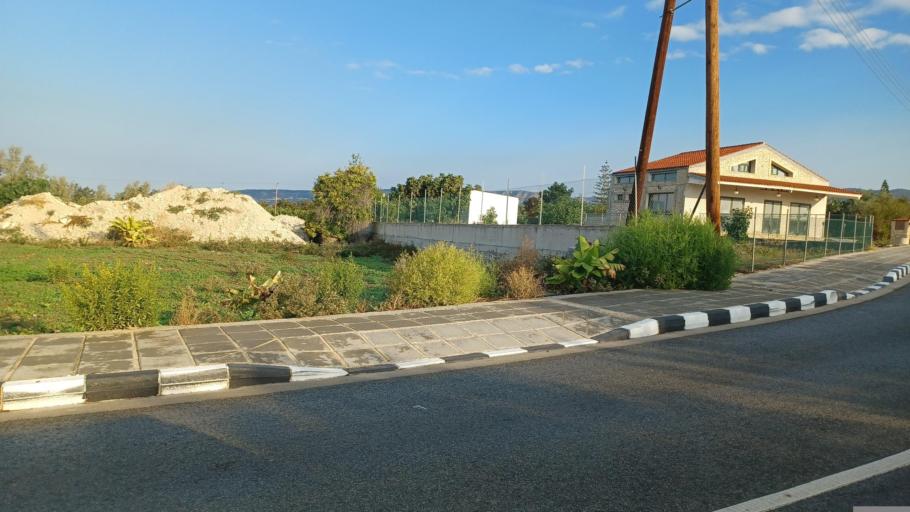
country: CY
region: Pafos
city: Kissonerga
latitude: 34.8259
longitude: 32.3967
